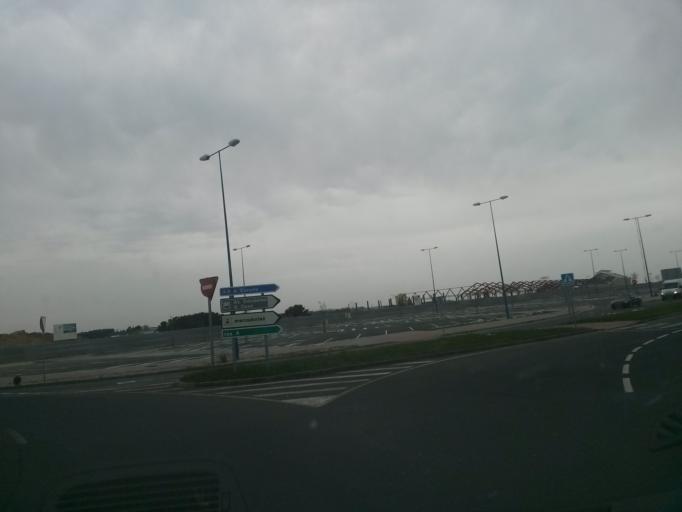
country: ES
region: Galicia
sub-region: Provincia de Lugo
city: Lugo
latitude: 43.0381
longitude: -7.5542
